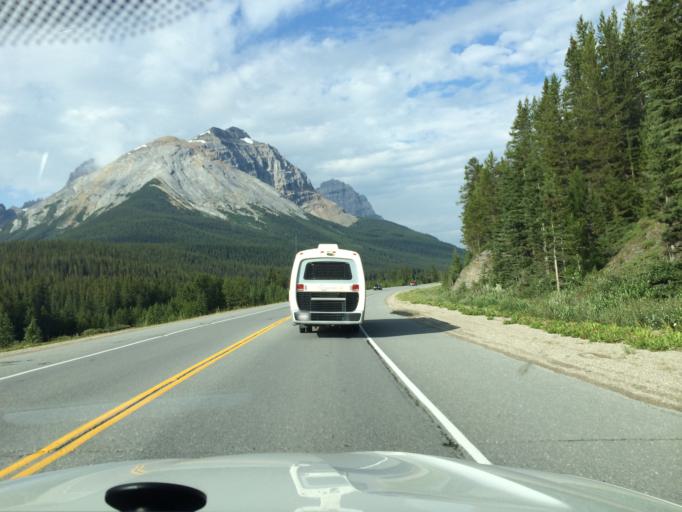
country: CA
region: Alberta
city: Lake Louise
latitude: 51.4439
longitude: -116.3370
